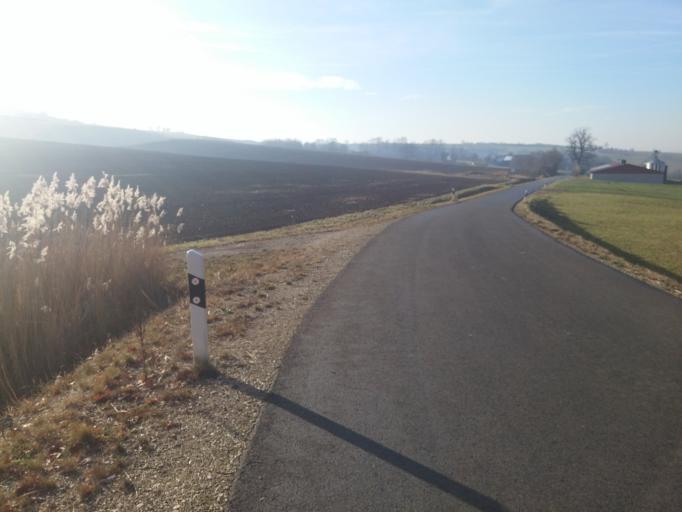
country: DE
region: Bavaria
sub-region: Upper Franconia
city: Untersiemau
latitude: 50.1723
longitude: 10.9721
